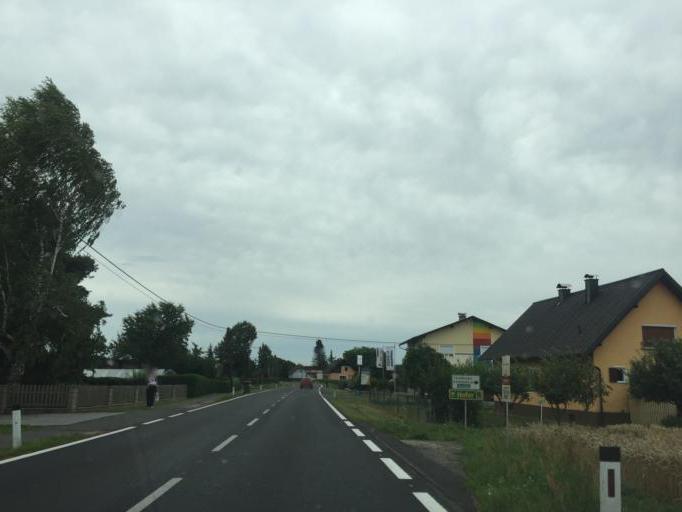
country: AT
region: Styria
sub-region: Politischer Bezirk Suedoststeiermark
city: Eichfeld
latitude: 46.7129
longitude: 15.7288
